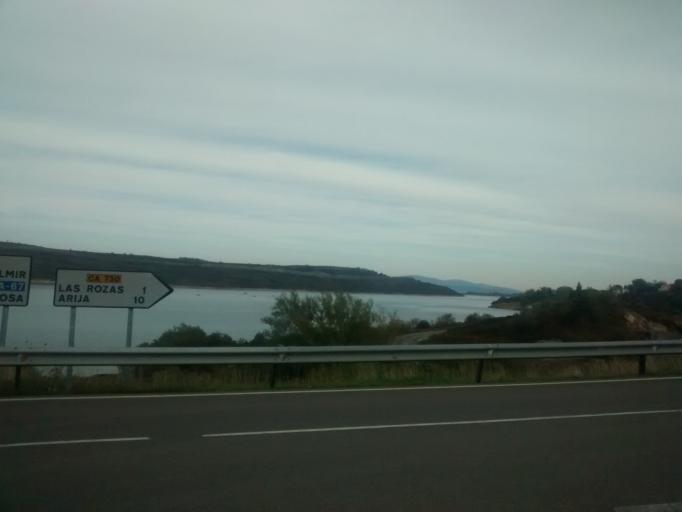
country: ES
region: Cantabria
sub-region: Provincia de Cantabria
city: San Miguel de Aguayo
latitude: 42.9707
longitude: -4.0462
